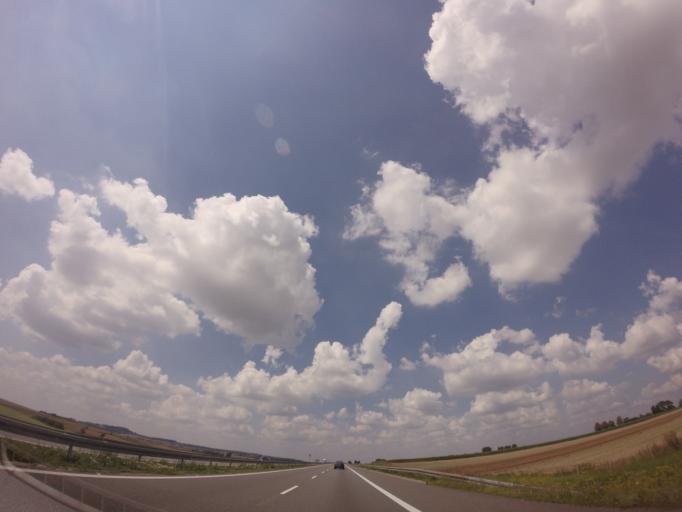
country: PL
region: Opole Voivodeship
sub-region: Powiat strzelecki
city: Lesnica
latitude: 50.4627
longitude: 18.2261
